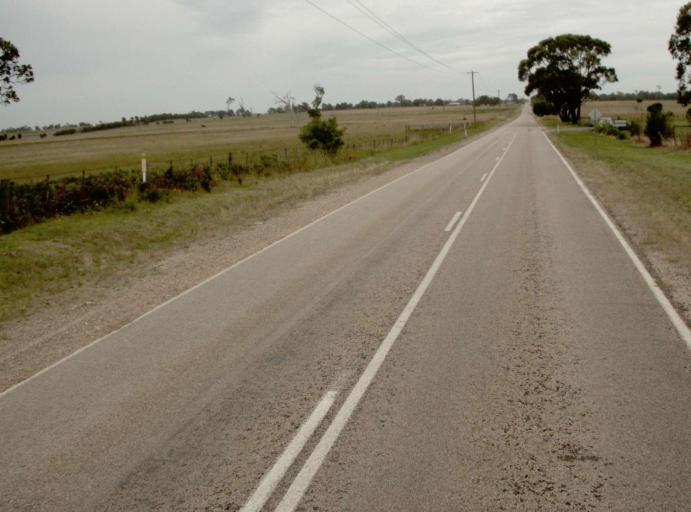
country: AU
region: Victoria
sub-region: East Gippsland
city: Bairnsdale
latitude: -37.8034
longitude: 147.4389
